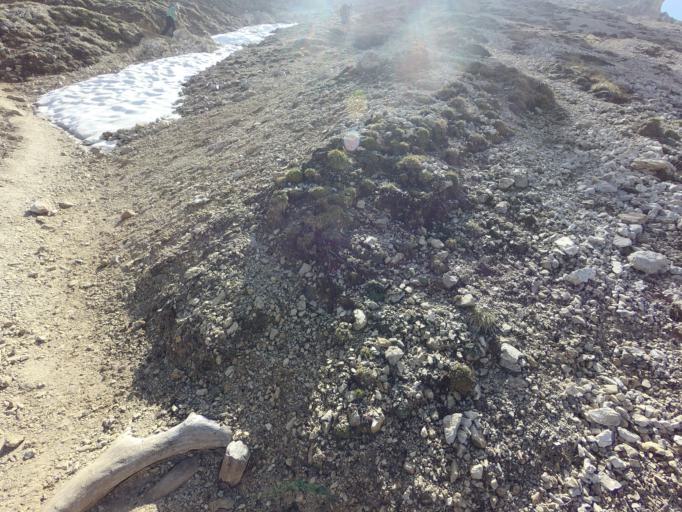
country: IT
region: Trentino-Alto Adige
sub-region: Provincia di Trento
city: Mazzin
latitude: 46.5024
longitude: 11.6369
